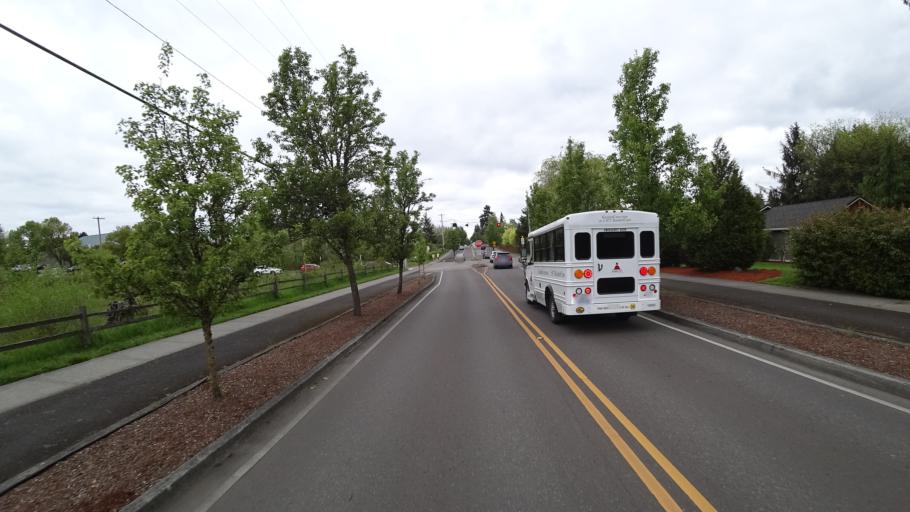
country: US
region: Oregon
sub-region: Washington County
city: Beaverton
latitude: 45.4580
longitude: -122.8364
